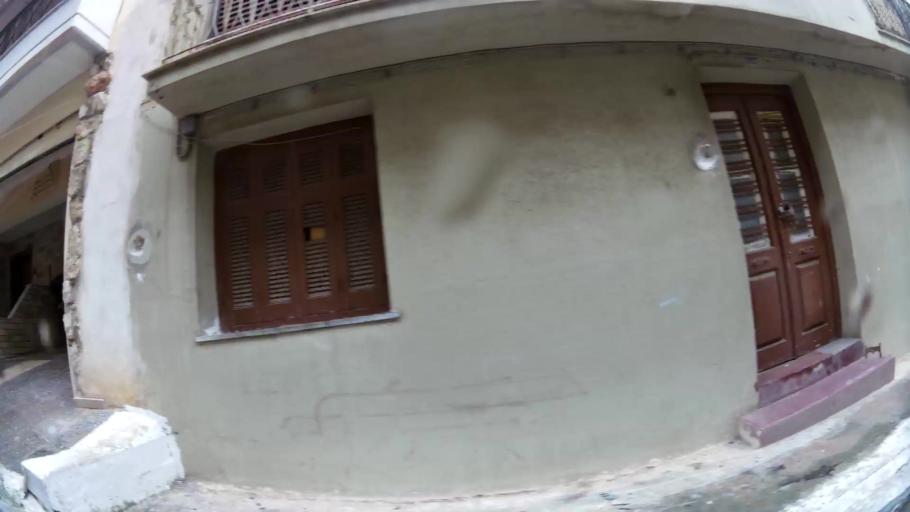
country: GR
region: Attica
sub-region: Nomos Piraios
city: Nikaia
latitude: 37.9592
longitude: 23.6463
